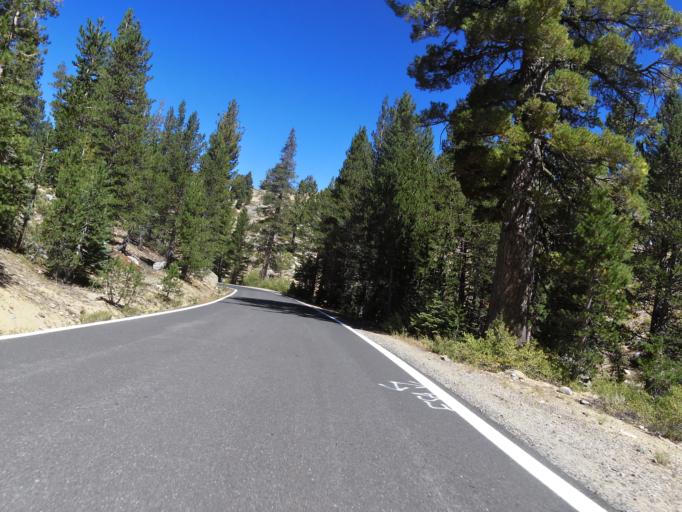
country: US
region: Nevada
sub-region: Douglas County
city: Gardnerville Ranchos
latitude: 38.5665
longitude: -119.8032
